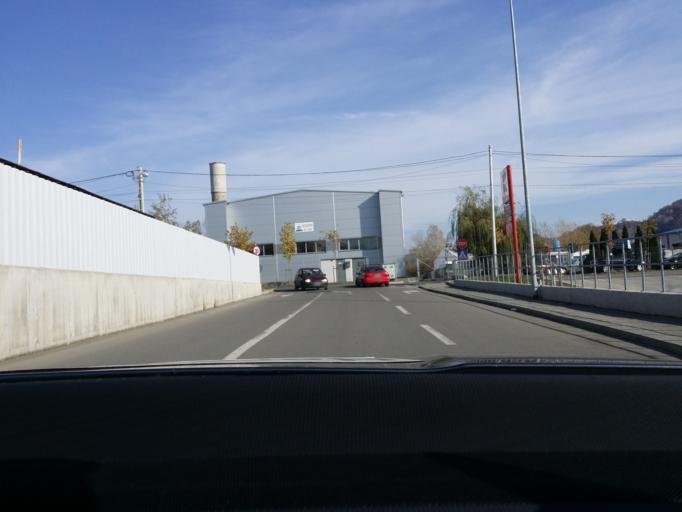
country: RO
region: Prahova
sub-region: Municipiul Campina
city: Campina
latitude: 45.1174
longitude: 25.7462
